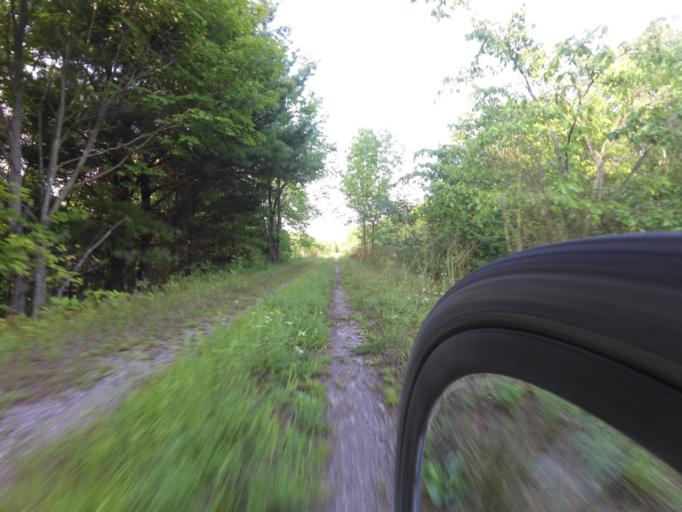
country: CA
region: Ontario
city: Kingston
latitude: 44.5202
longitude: -76.4153
